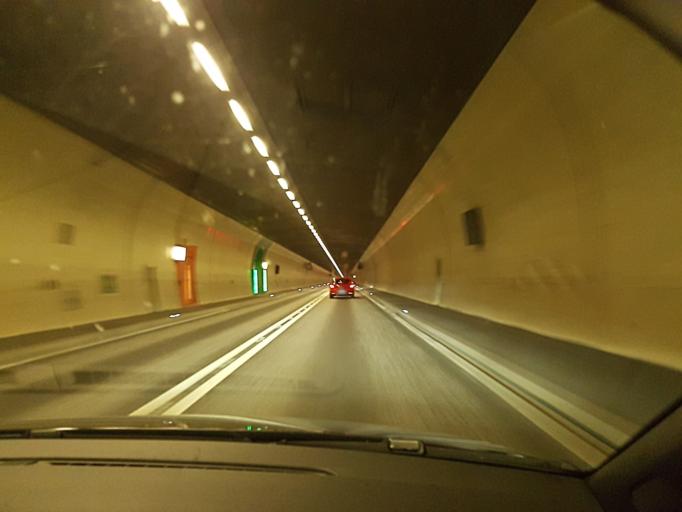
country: CH
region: Grisons
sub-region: Praettigau/Davos District
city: Klosters Serneus
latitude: 46.8723
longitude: 9.8665
